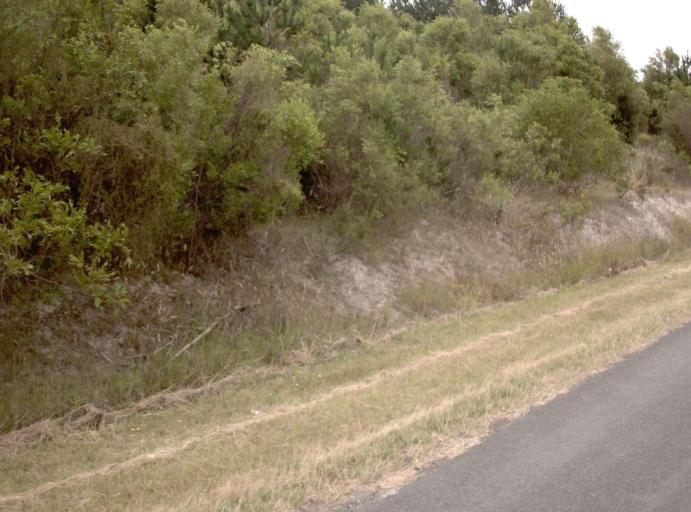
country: AU
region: Victoria
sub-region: Latrobe
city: Morwell
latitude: -38.2925
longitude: 146.2946
